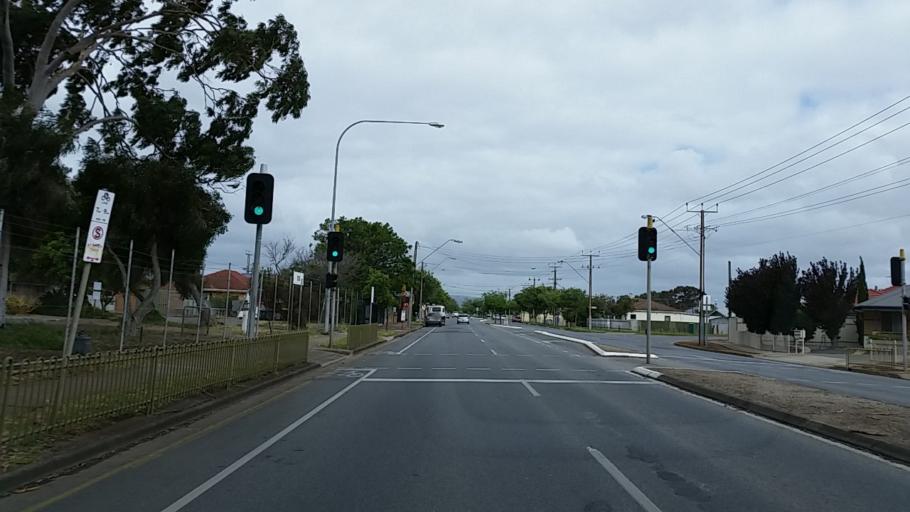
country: AU
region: South Australia
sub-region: Charles Sturt
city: Findon
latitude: -34.8988
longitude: 138.5374
